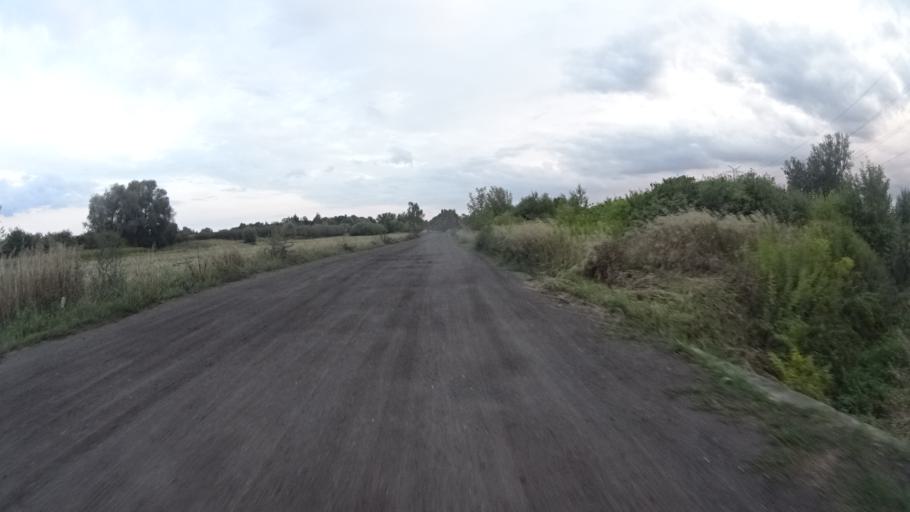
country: PL
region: Masovian Voivodeship
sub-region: Powiat warszawski zachodni
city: Ozarow Mazowiecki
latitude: 52.2351
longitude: 20.7656
